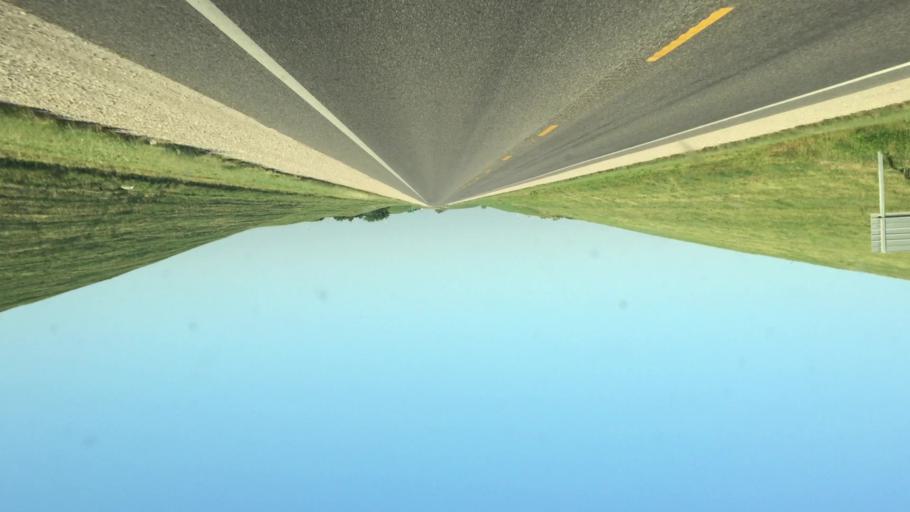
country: US
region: Kansas
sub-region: Doniphan County
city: Troy
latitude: 39.7962
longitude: -95.1072
